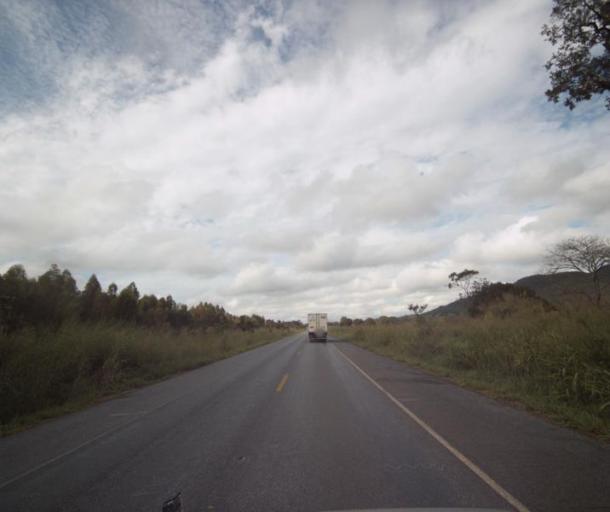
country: BR
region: Goias
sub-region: Pirenopolis
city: Pirenopolis
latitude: -15.5123
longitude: -48.6224
